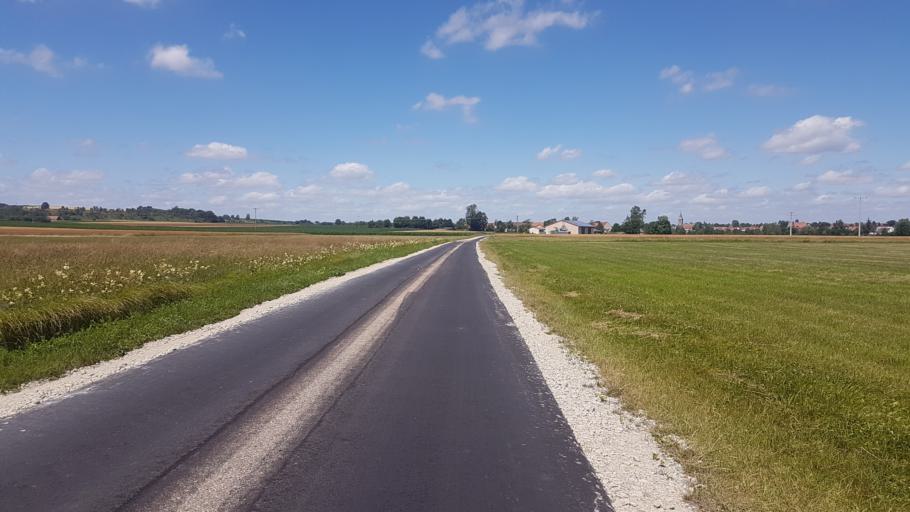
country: DE
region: Bavaria
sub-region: Regierungsbezirk Mittelfranken
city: Leutershausen
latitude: 49.2881
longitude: 10.4122
